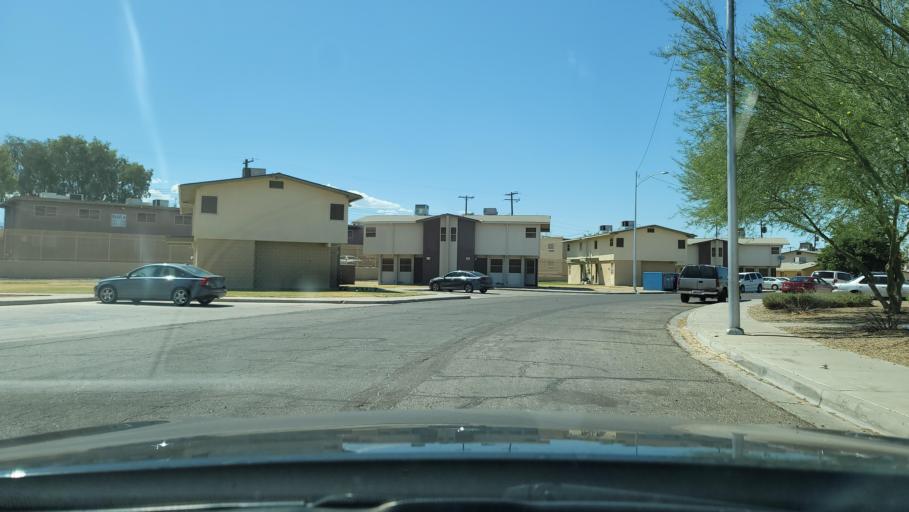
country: US
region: Nevada
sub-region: Clark County
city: Las Vegas
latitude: 36.1900
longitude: -115.1542
